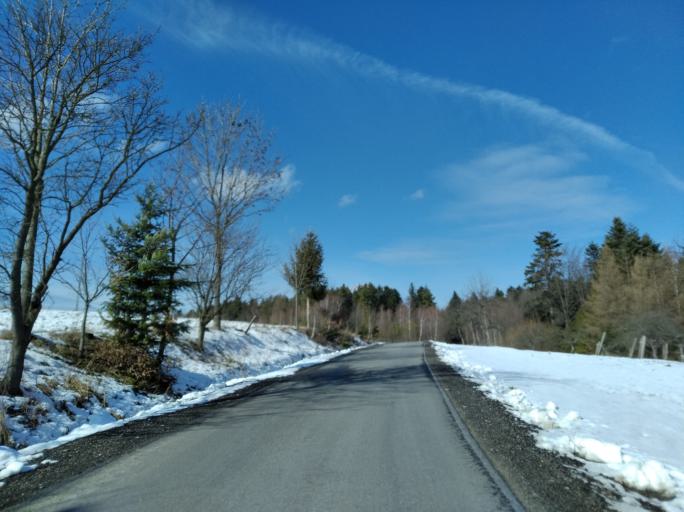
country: PL
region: Subcarpathian Voivodeship
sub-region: Powiat krosnienski
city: Korczyna
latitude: 49.7324
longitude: 21.8581
